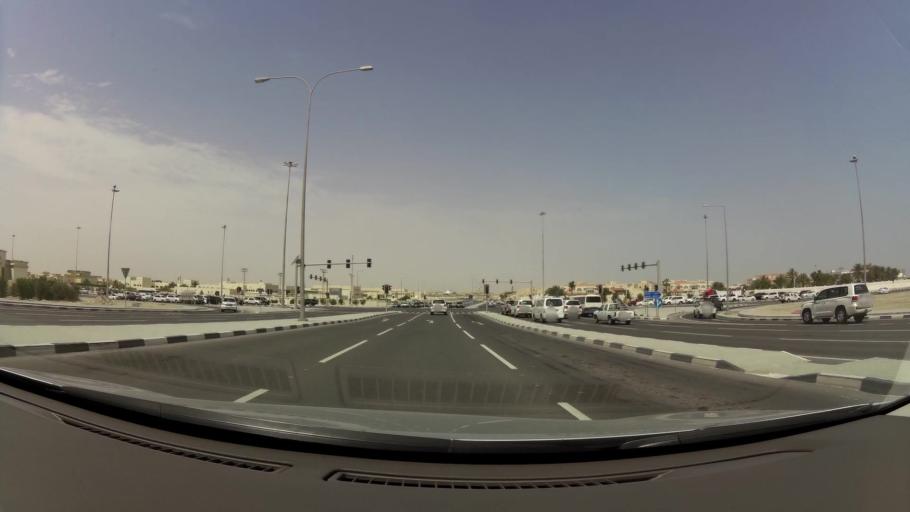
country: QA
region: Baladiyat ar Rayyan
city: Ar Rayyan
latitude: 25.3484
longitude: 51.4790
